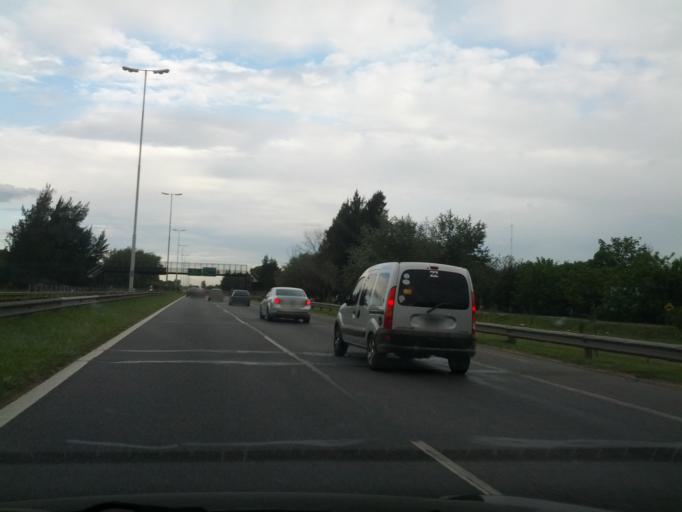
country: AR
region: Buenos Aires
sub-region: Partido de General Rodriguez
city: General Rodriguez
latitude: -34.5902
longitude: -58.9614
